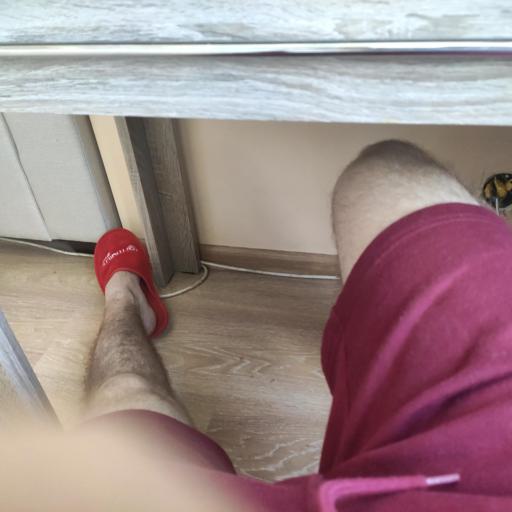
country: RU
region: Moscow
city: Khimki
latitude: 55.9208
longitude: 37.4446
